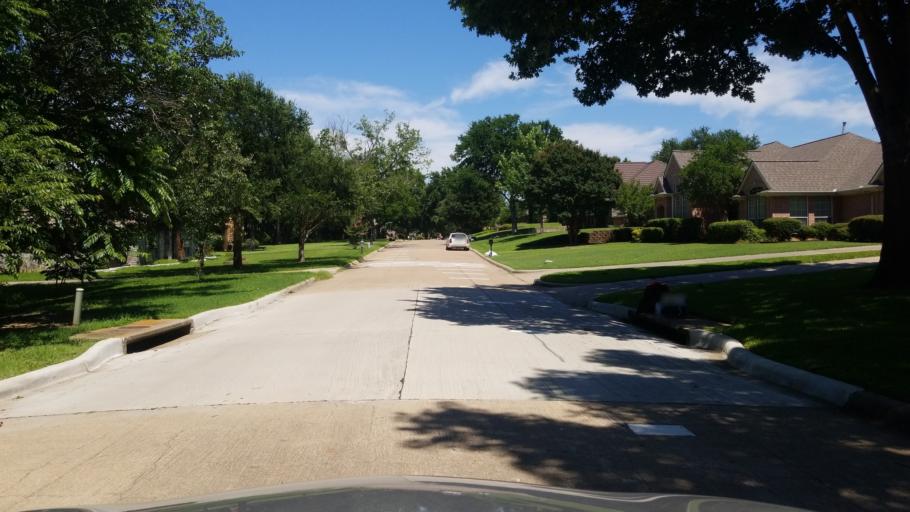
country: US
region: Texas
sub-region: Dallas County
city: Grand Prairie
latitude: 32.6872
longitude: -97.0022
